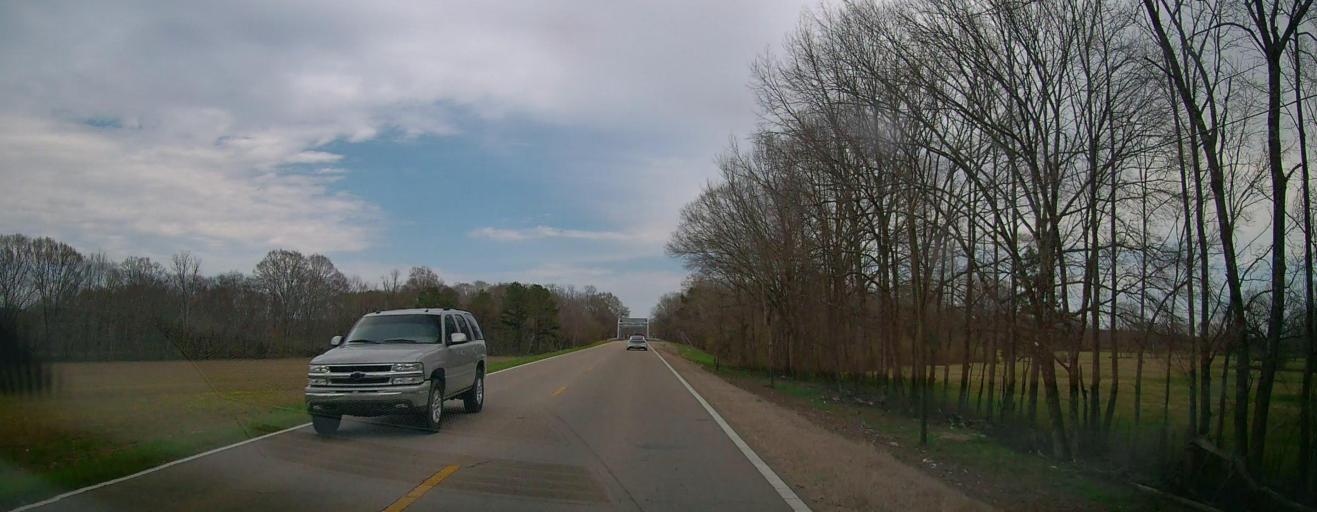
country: US
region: Mississippi
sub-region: Itawamba County
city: Mantachie
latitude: 34.2530
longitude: -88.4792
